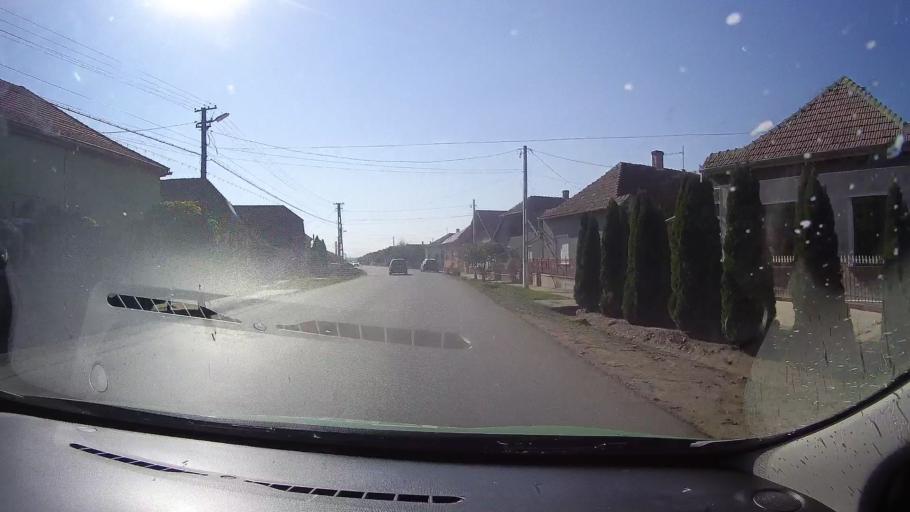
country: RO
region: Satu Mare
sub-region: Comuna Camin
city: Camin
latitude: 47.7276
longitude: 22.4767
